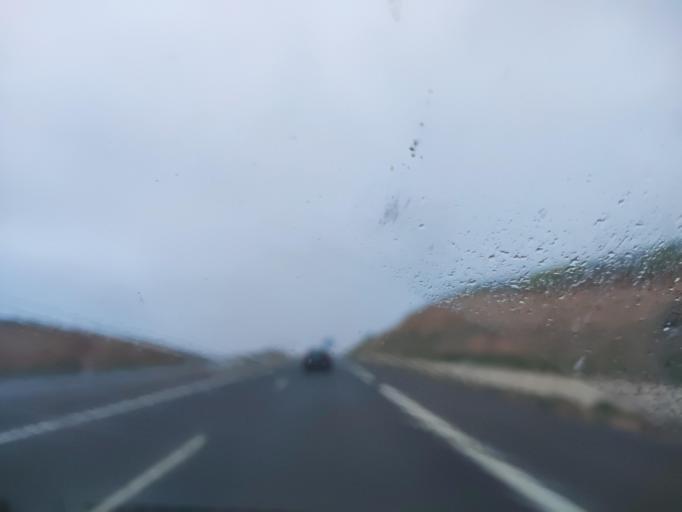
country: ES
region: Castille-La Mancha
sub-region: Province of Toledo
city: Bargas
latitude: 39.9110
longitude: -4.0554
